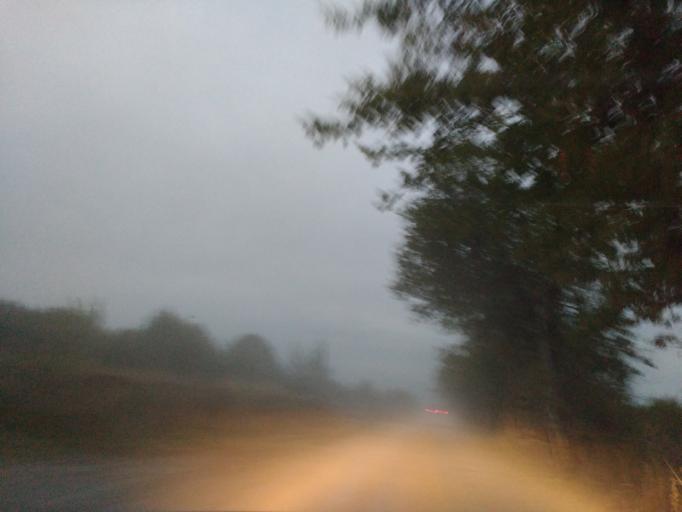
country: DE
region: North Rhine-Westphalia
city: Warstein
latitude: 51.4291
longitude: 8.3687
